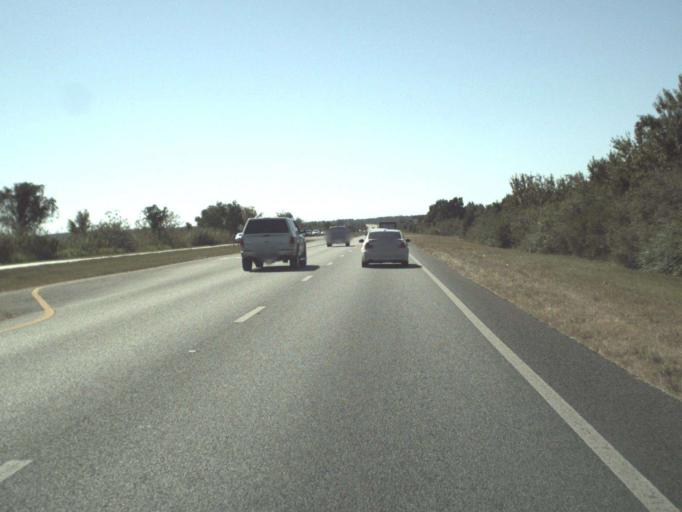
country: US
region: Florida
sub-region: Santa Rosa County
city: Pace
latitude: 30.5663
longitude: -87.1874
